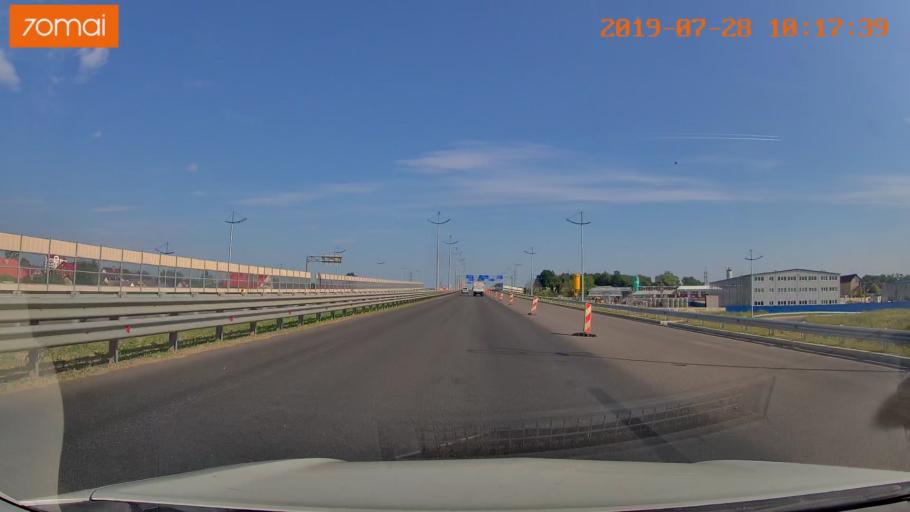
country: RU
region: Kaliningrad
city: Maloye Isakovo
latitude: 54.7424
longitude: 20.5932
